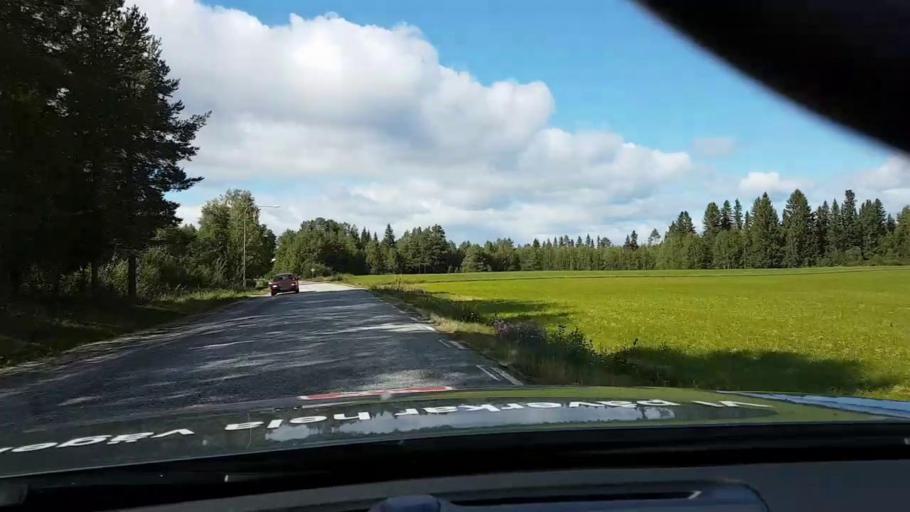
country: SE
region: Vaesterbotten
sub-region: Asele Kommun
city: Asele
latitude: 63.9351
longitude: 17.2889
